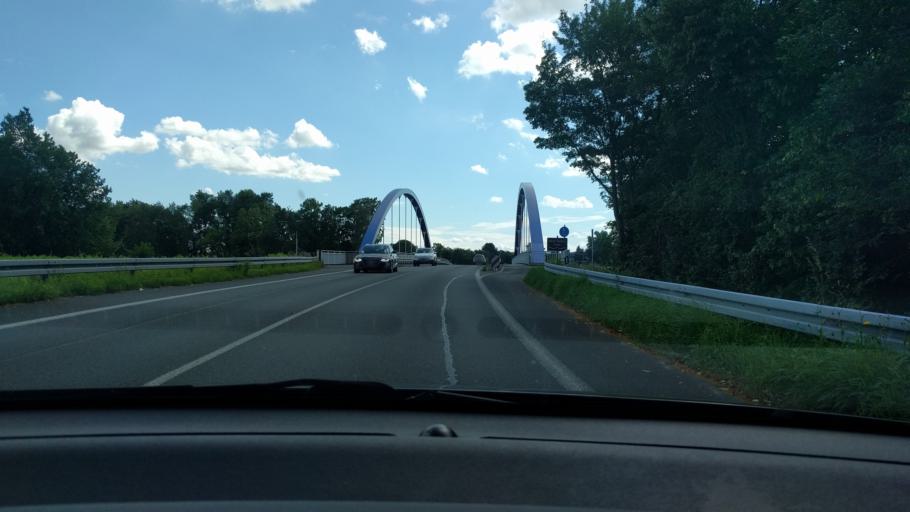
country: DE
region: North Rhine-Westphalia
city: Olfen
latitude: 51.6943
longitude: 7.3134
